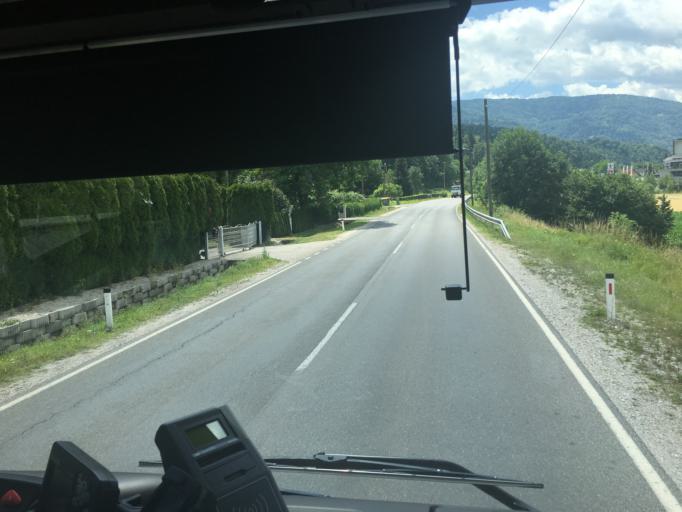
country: SI
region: Ruse
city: Ruse
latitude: 46.5426
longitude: 15.5223
